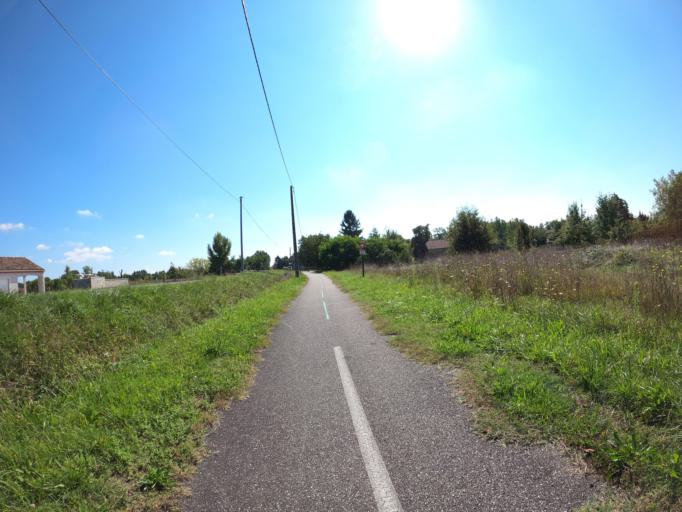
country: FR
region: Aquitaine
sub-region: Departement du Lot-et-Garonne
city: Bias
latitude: 44.4201
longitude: 0.6568
